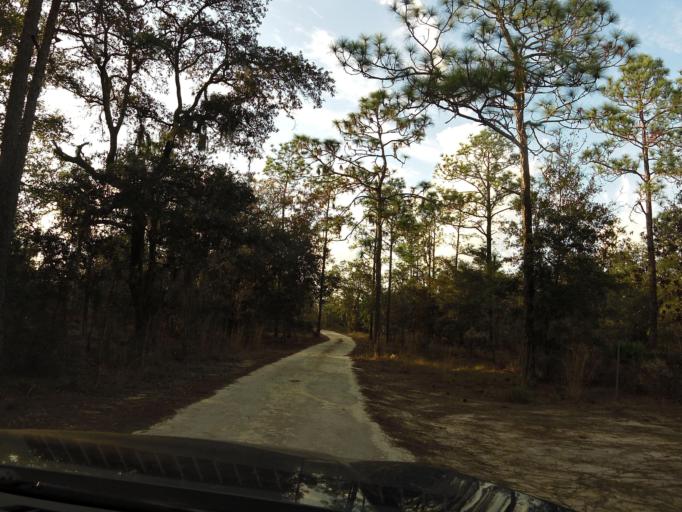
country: US
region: Florida
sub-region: Clay County
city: Middleburg
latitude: 30.1317
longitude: -81.9472
